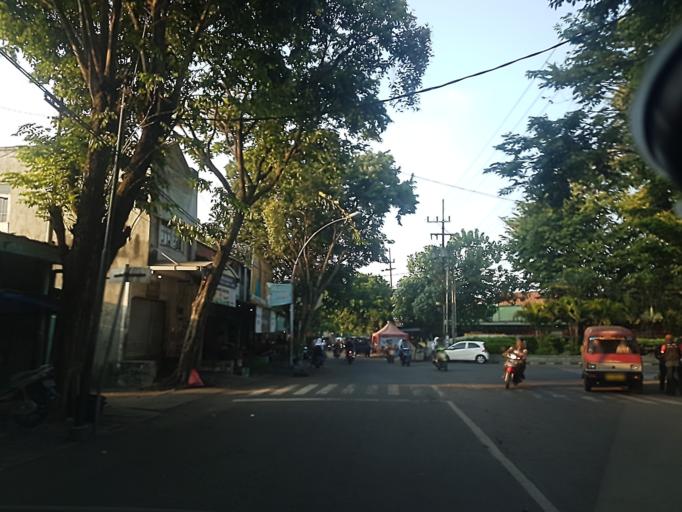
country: ID
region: East Java
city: Gresik
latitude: -7.1544
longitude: 112.6582
